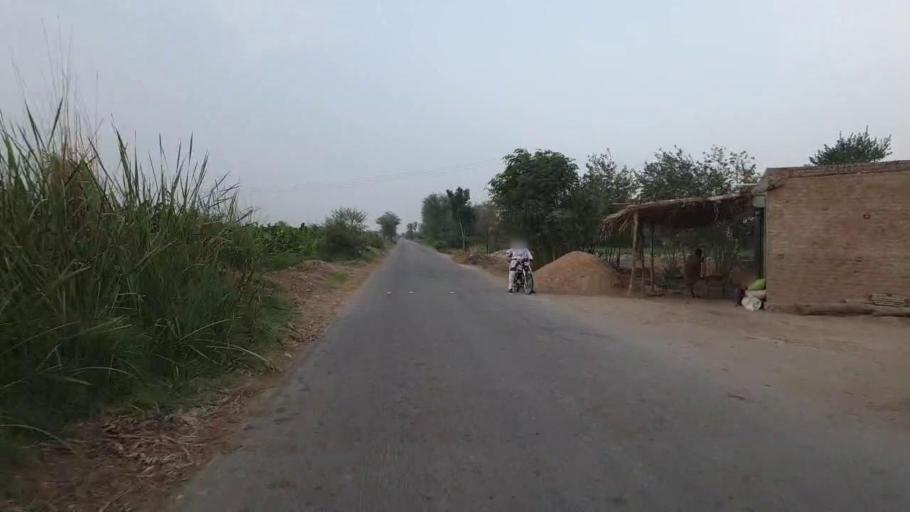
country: PK
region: Sindh
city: Daur
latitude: 26.4144
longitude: 68.2415
